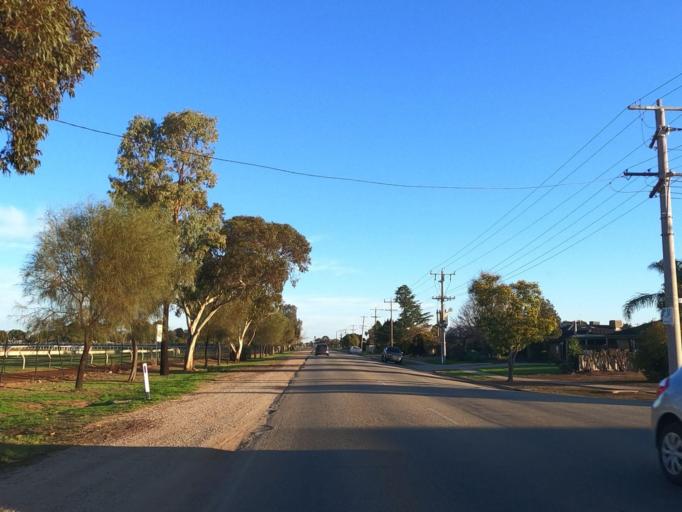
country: AU
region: Victoria
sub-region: Swan Hill
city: Swan Hill
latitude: -35.3508
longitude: 143.5542
